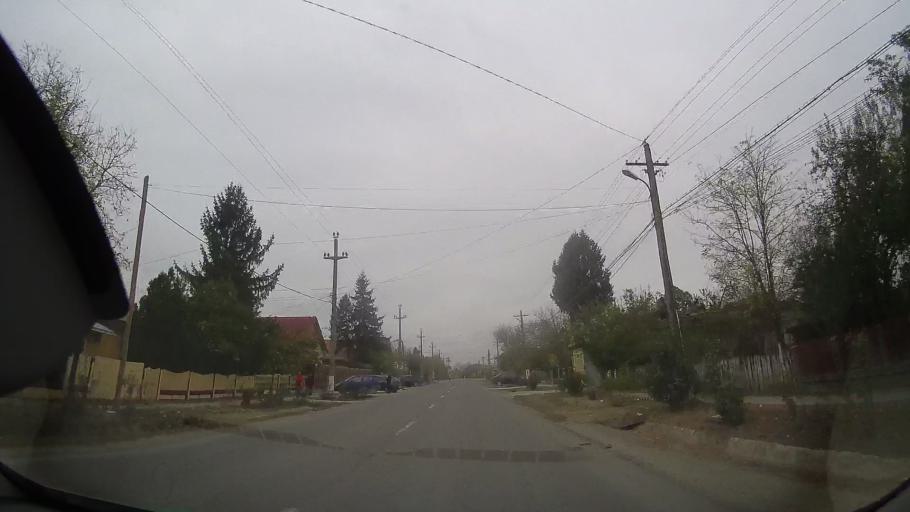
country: RO
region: Ialomita
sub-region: Comuna Grivita
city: Grivita
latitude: 44.7341
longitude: 27.2945
